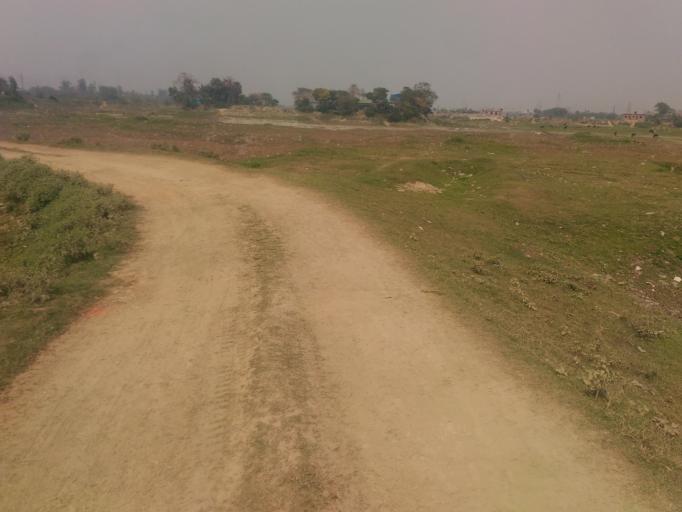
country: BD
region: Dhaka
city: Narayanganj
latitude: 23.6399
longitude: 90.4466
